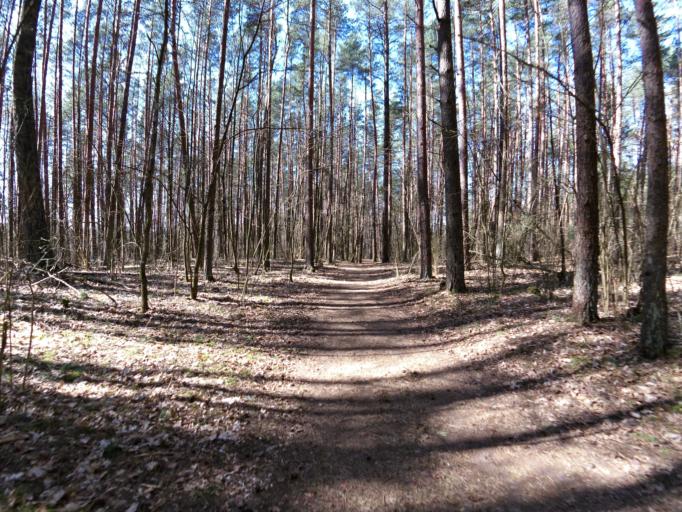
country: LT
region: Vilnius County
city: Pilaite
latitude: 54.6951
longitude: 25.1918
